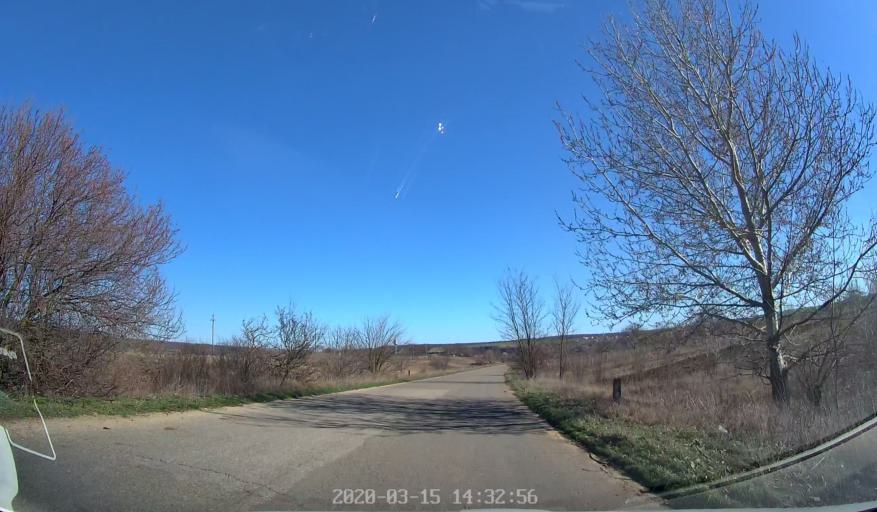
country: MD
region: Orhei
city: Orhei
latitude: 47.3417
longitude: 28.9135
